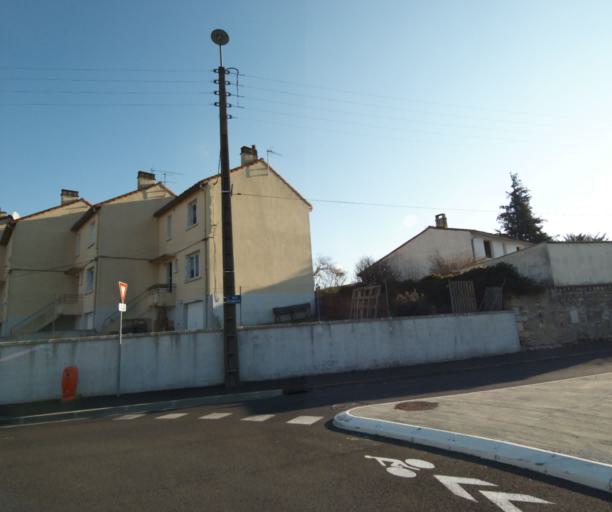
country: FR
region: Poitou-Charentes
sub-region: Departement des Deux-Sevres
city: Niort
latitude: 46.3421
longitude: -0.4523
